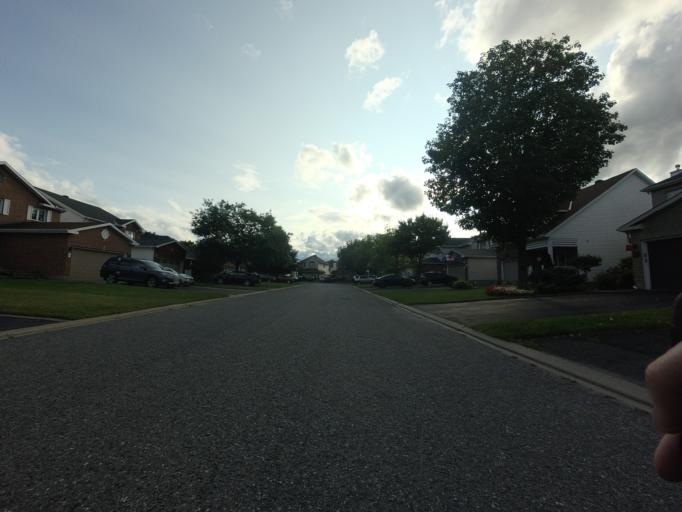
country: CA
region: Ontario
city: Bells Corners
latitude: 45.2849
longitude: -75.7195
